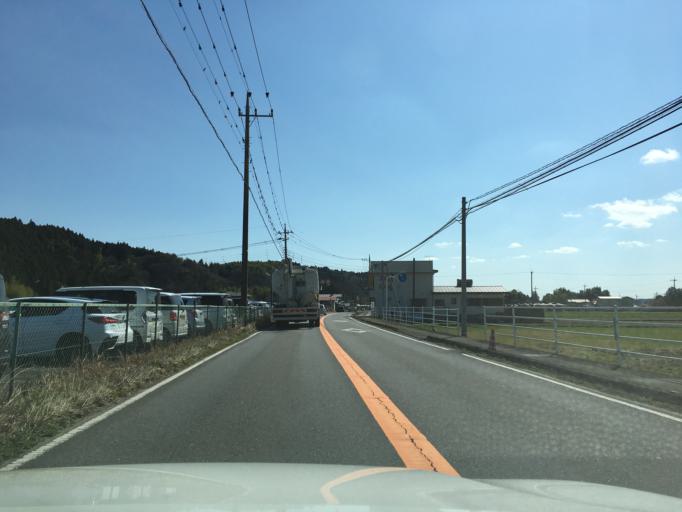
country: JP
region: Tochigi
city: Otawara
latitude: 36.8788
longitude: 140.1197
